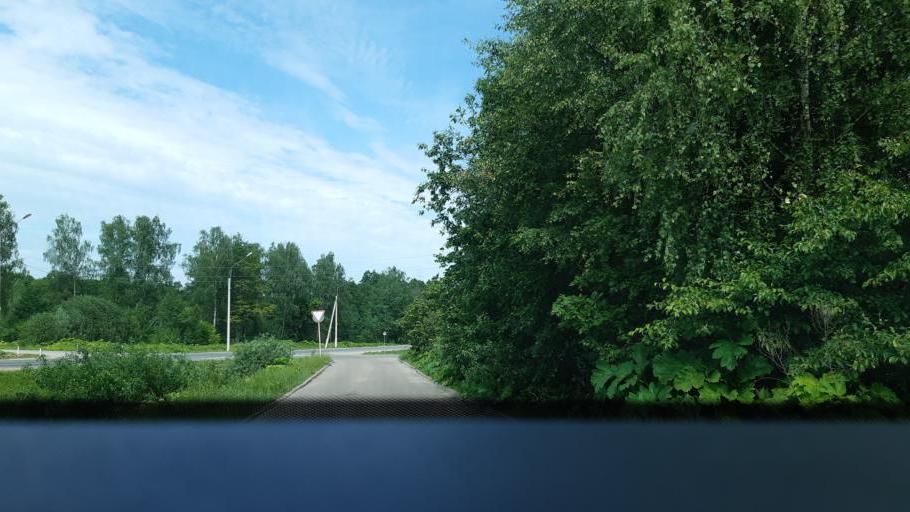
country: RU
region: Kaluga
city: Myatlevo
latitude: 54.9045
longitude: 35.6844
